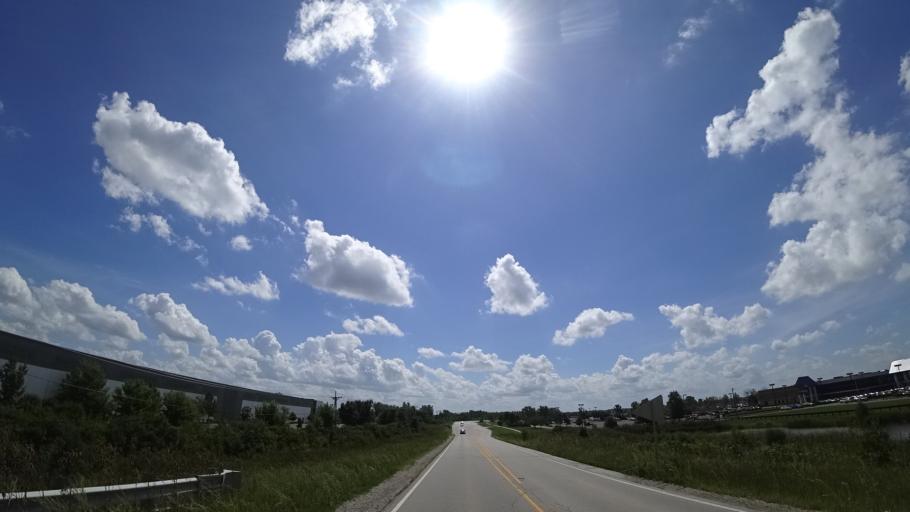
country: US
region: Illinois
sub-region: Cook County
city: Tinley Park
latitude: 41.5500
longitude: -87.7835
